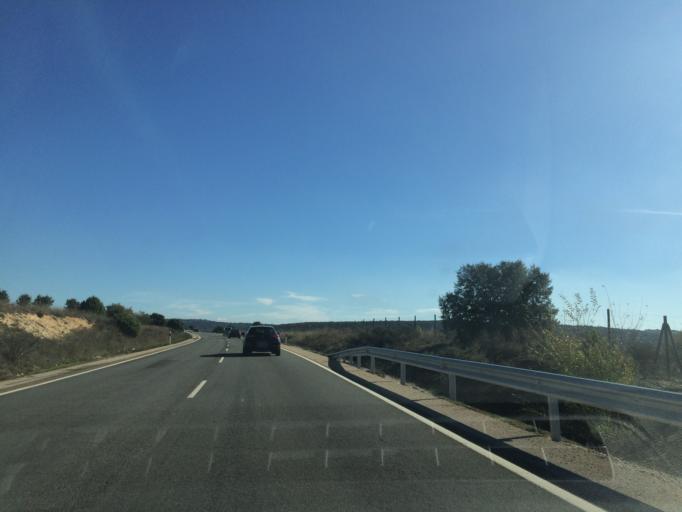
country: ES
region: Madrid
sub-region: Provincia de Madrid
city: Venturada
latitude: 40.7806
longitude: -3.6517
